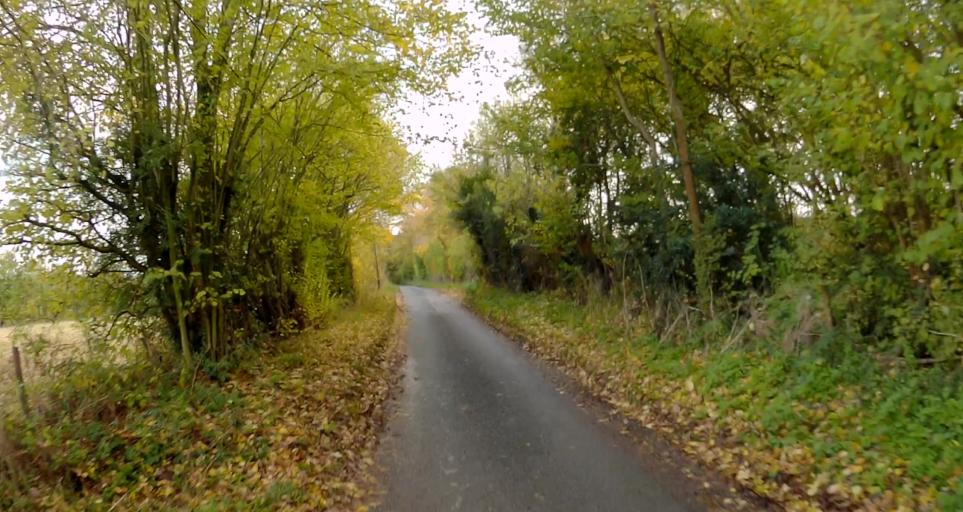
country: GB
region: England
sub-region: Hampshire
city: Long Sutton
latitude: 51.2156
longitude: -0.9636
